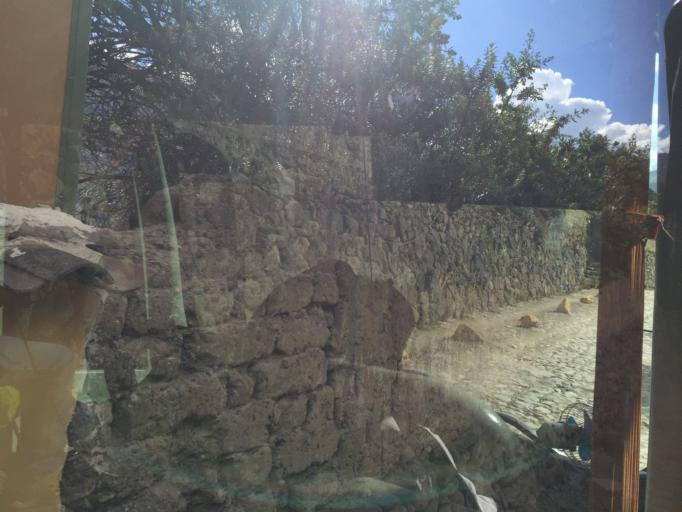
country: PE
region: Cusco
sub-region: Provincia de Urubamba
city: Ollantaytambo
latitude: -13.2588
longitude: -72.2620
